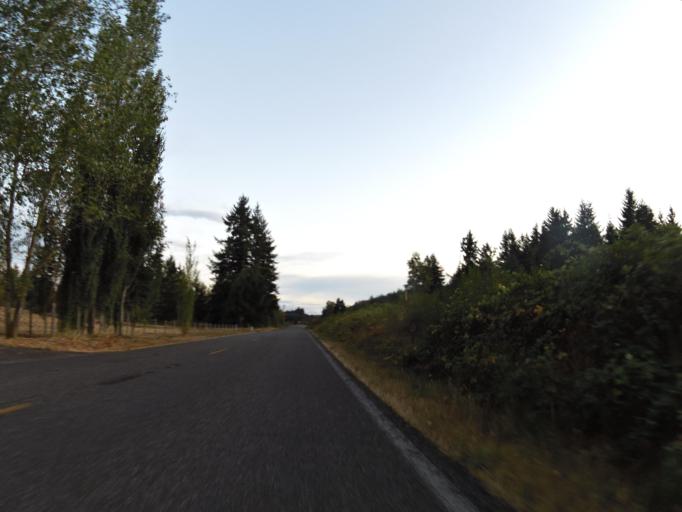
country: US
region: Washington
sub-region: Thurston County
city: Tenino
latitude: 46.8226
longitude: -122.8617
